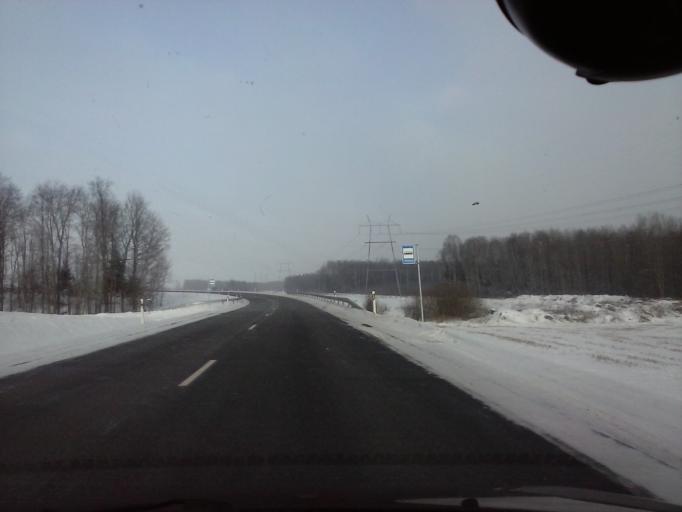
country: EE
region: Viljandimaa
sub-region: Abja vald
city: Abja-Paluoja
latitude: 58.2894
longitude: 25.2942
